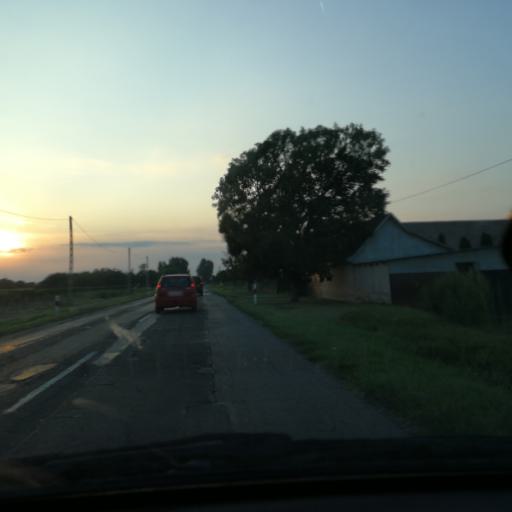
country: HU
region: Bacs-Kiskun
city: Soltvadkert
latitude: 46.5920
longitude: 19.3380
